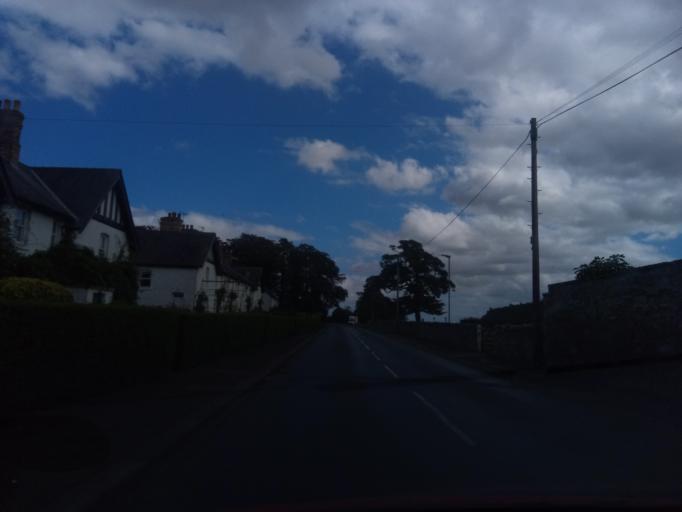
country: GB
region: Scotland
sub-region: The Scottish Borders
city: Coldstream
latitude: 55.6383
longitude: -2.3221
